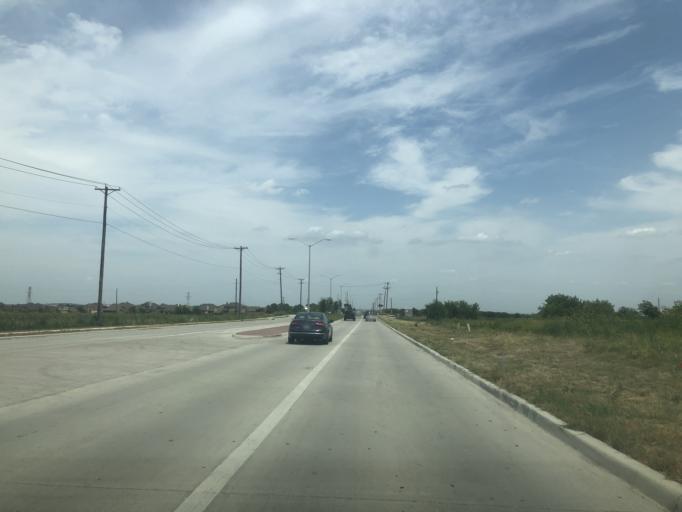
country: US
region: Texas
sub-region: Tarrant County
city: Saginaw
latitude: 32.8837
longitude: -97.3649
